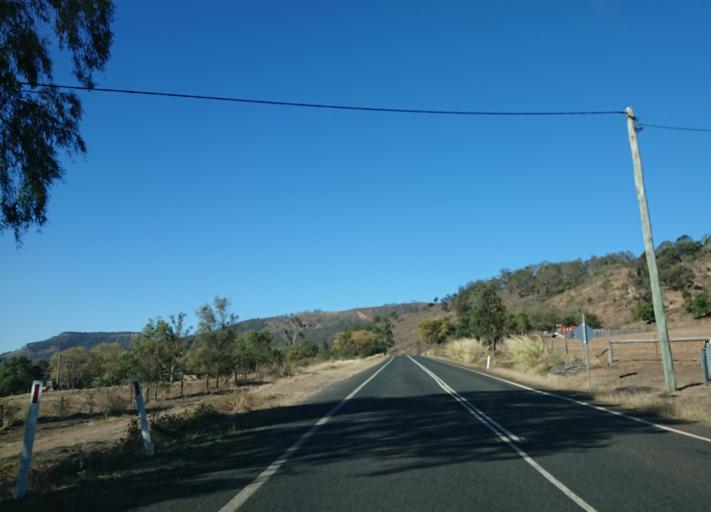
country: AU
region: Queensland
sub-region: Toowoomba
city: Rangeville
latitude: -27.7195
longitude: 152.1192
